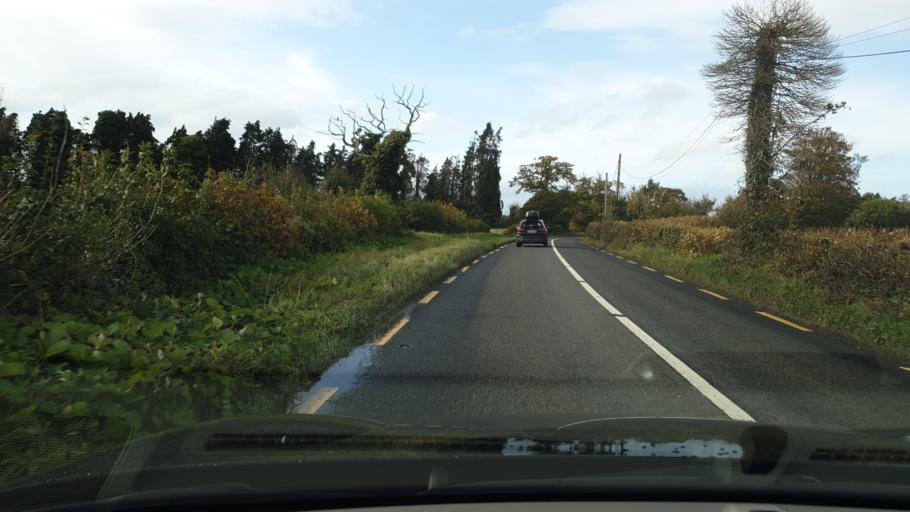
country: IE
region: Leinster
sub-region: An Mhi
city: Ratoath
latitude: 53.5181
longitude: -6.5001
